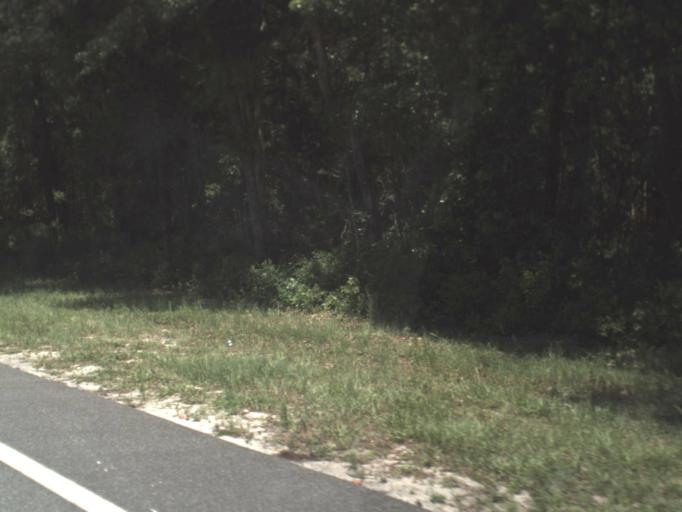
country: US
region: Florida
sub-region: Dixie County
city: Cross City
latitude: 29.8483
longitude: -82.9651
